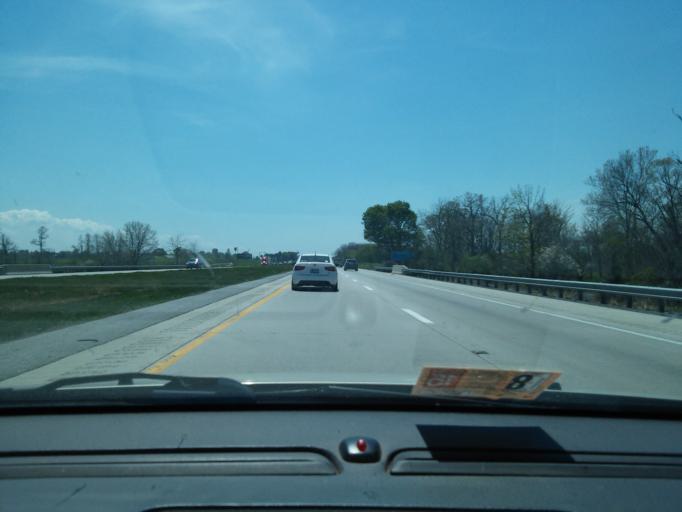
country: US
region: Pennsylvania
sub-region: Franklin County
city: Scotland
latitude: 39.9724
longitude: -77.5736
